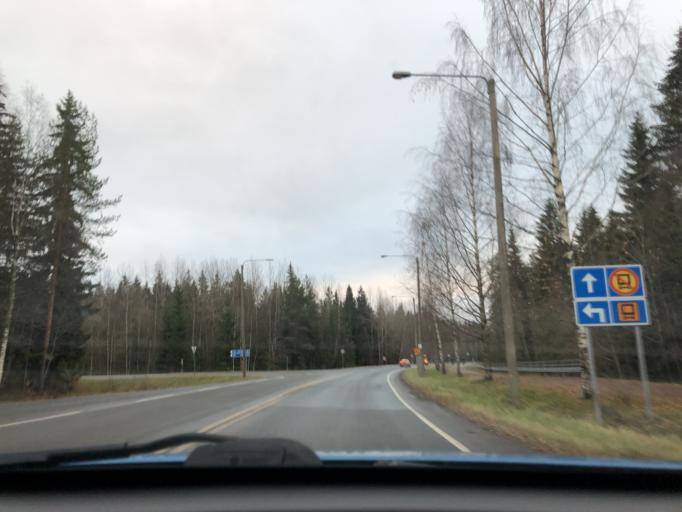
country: FI
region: Pirkanmaa
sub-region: Tampere
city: Kangasala
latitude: 61.5322
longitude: 23.9519
